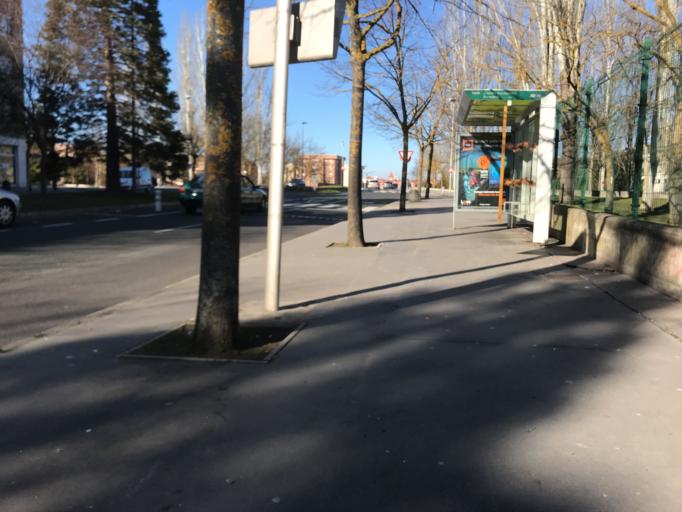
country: ES
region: Basque Country
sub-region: Provincia de Alava
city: Gasteiz / Vitoria
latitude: 42.8442
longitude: -2.6916
